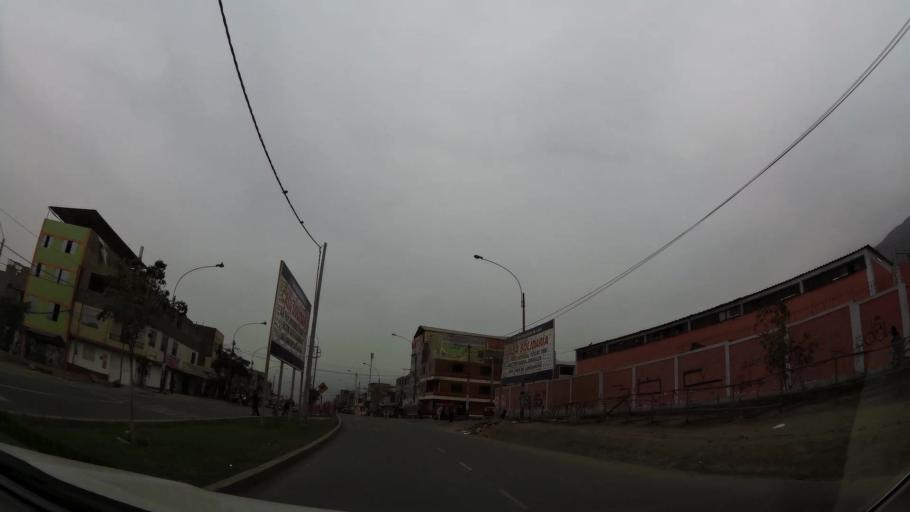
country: PE
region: Lima
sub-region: Lima
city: Independencia
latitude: -11.9582
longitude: -77.0047
